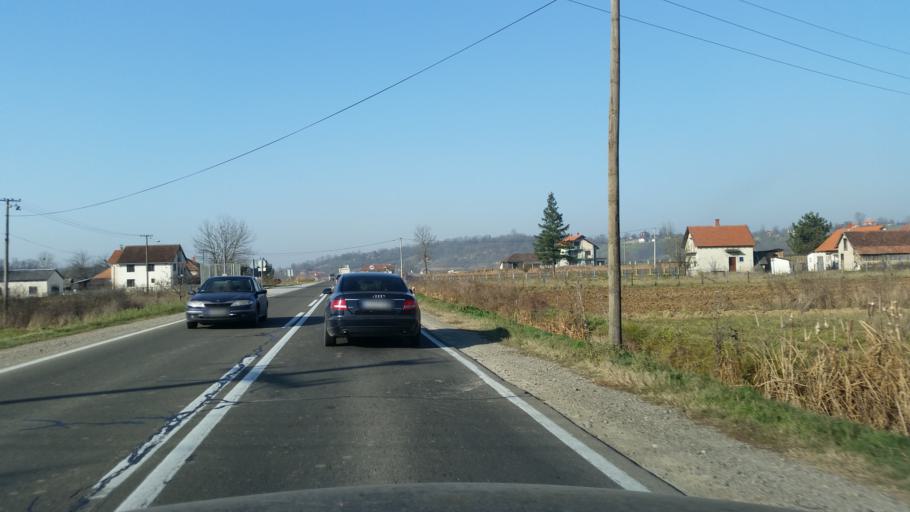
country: RS
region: Central Serbia
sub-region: Belgrade
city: Lazarevac
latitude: 44.3116
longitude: 20.2422
